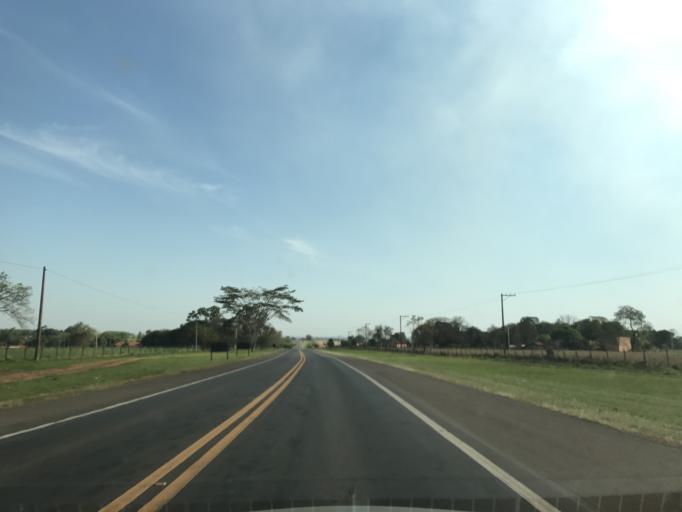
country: BR
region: Sao Paulo
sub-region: Penapolis
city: Penapolis
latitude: -21.3998
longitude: -50.1107
